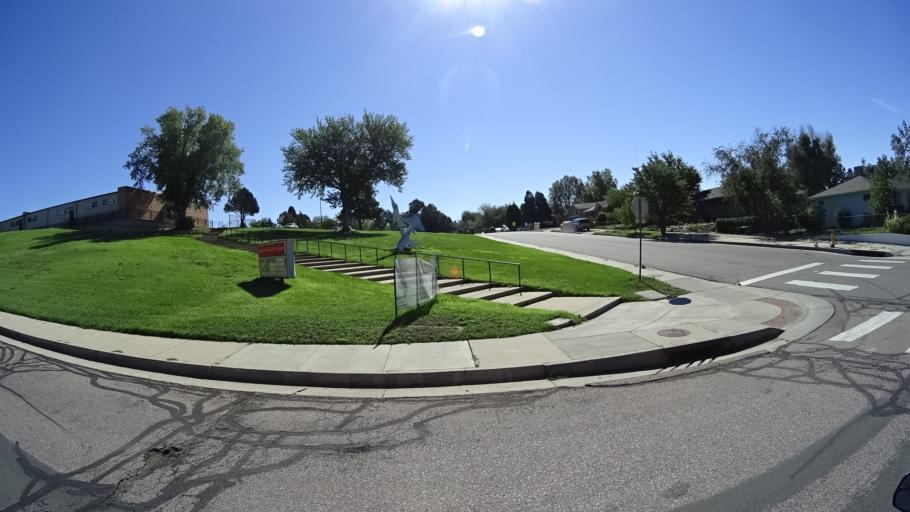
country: US
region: Colorado
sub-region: El Paso County
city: Colorado Springs
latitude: 38.8571
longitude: -104.7827
